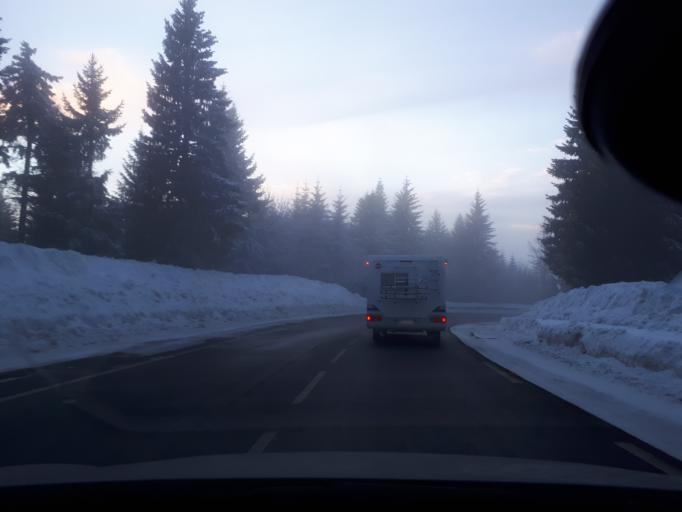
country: FR
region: Rhone-Alpes
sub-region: Departement de l'Isere
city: Vaulnaveys-le-Bas
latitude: 45.1011
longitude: 5.8613
